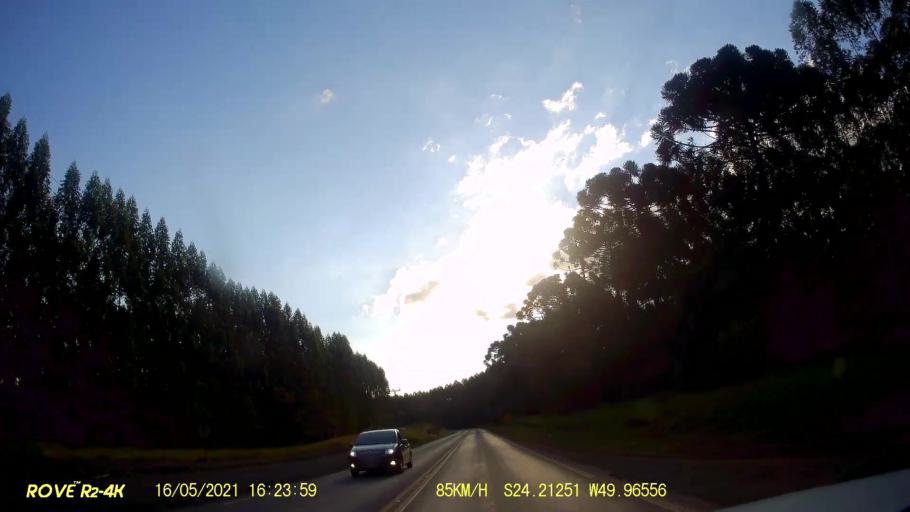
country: BR
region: Parana
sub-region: Jaguariaiva
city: Jaguariaiva
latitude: -24.2125
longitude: -49.9657
